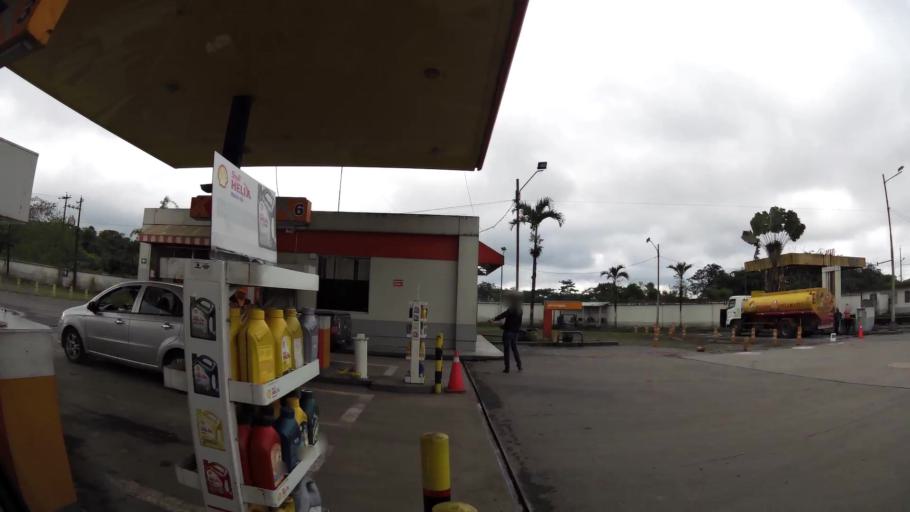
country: EC
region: Santo Domingo de los Tsachilas
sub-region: Canton Santo Domingo de los Colorados
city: Santo Domingo de los Colorados
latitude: -0.2636
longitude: -79.1138
